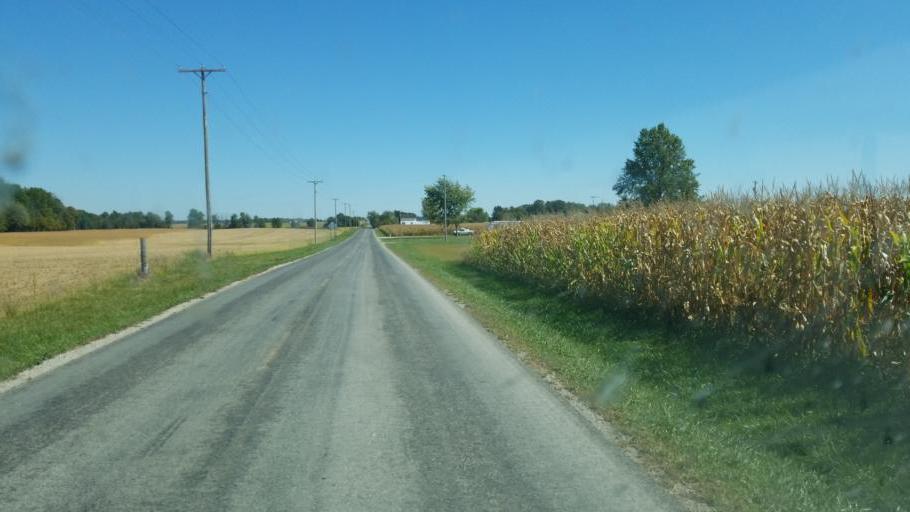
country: US
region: Ohio
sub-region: Huron County
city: Plymouth
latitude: 40.9944
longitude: -82.6005
